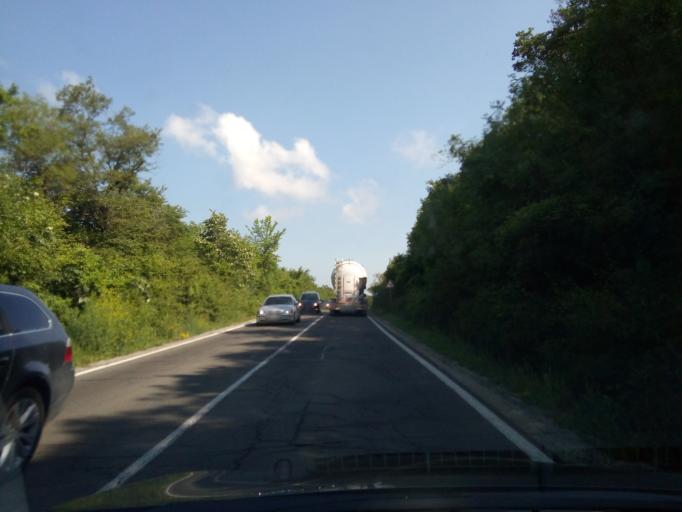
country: BG
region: Burgas
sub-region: Obshtina Nesebur
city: Sveti Vlas
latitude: 42.7545
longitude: 27.7551
